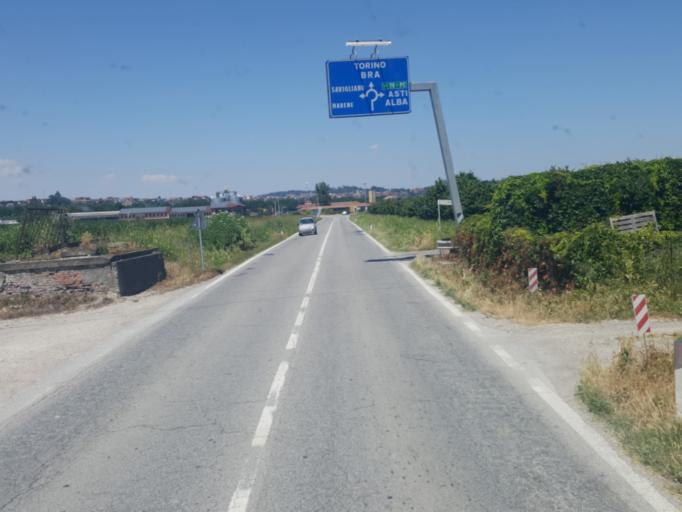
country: IT
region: Piedmont
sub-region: Provincia di Cuneo
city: Cherasco
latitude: 44.6637
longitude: 7.8545
